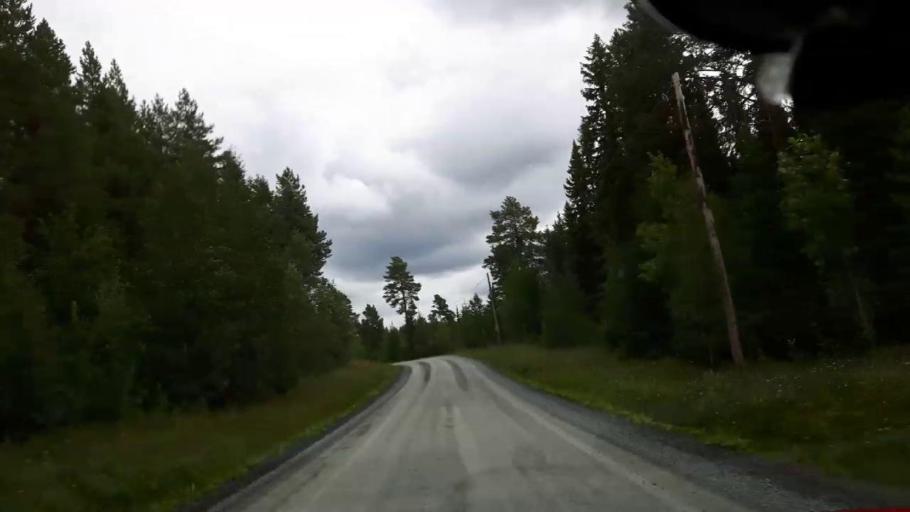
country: SE
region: Jaemtland
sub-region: Krokoms Kommun
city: Krokom
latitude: 63.5768
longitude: 14.2262
